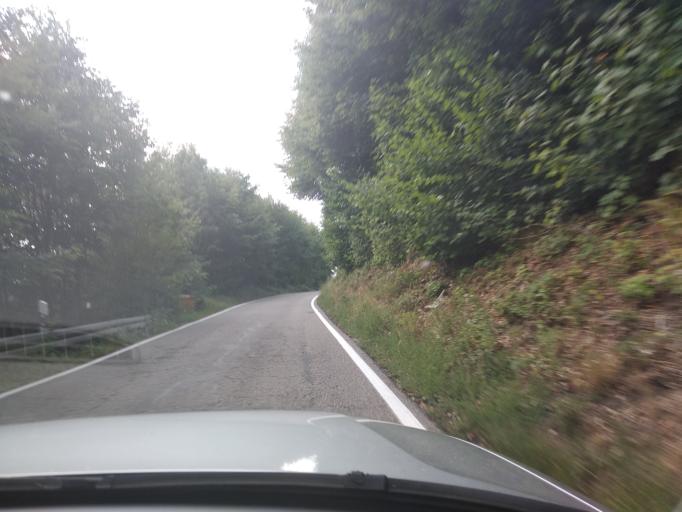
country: DE
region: Baden-Wuerttemberg
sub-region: Tuebingen Region
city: Aichstetten
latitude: 47.9046
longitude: 10.0396
